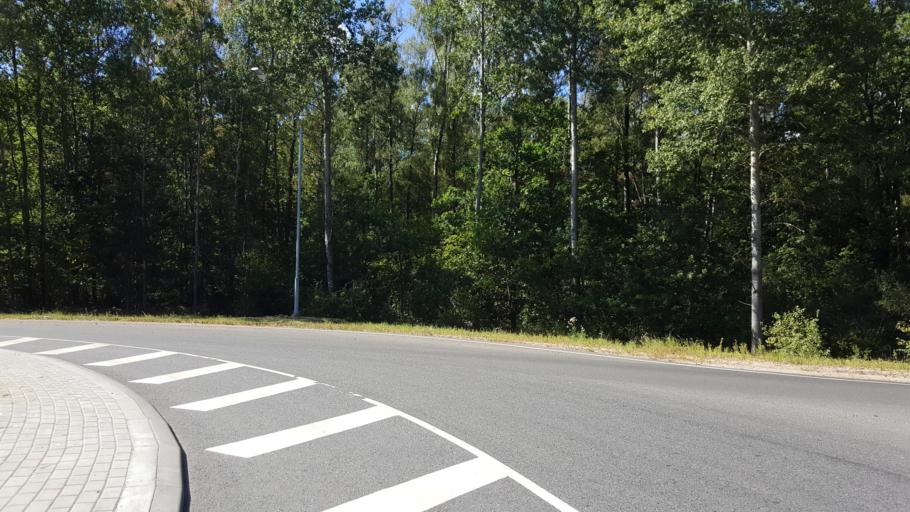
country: BY
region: Brest
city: Vysokaye
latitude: 52.3521
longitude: 23.4062
